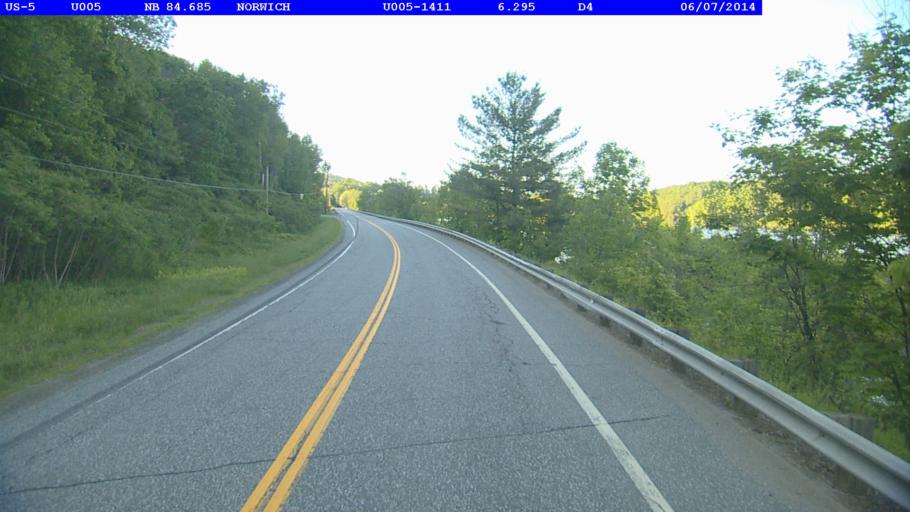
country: US
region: New Hampshire
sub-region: Grafton County
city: Hanover
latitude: 43.7507
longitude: -72.2313
